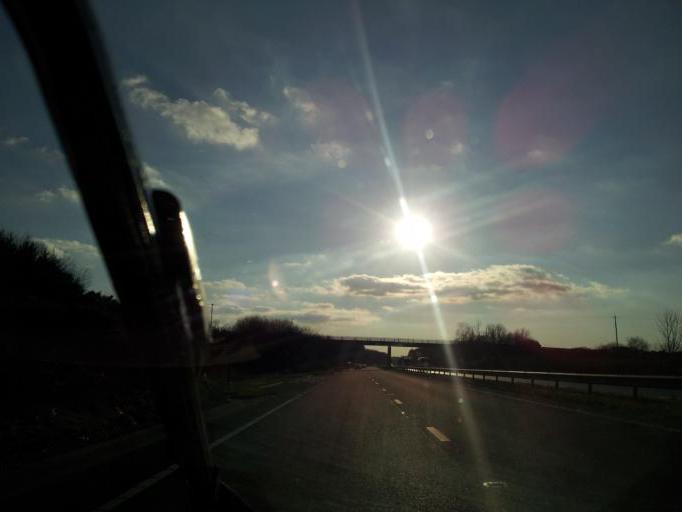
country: GB
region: England
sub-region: Devon
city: Okehampton
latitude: 50.6960
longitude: -4.1251
